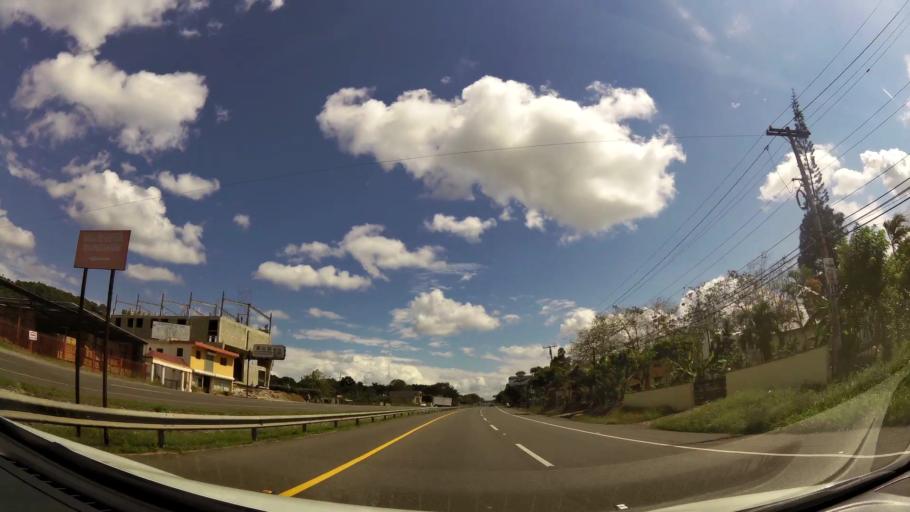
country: DO
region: La Vega
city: Rio Verde Arriba
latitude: 19.2963
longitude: -70.5785
